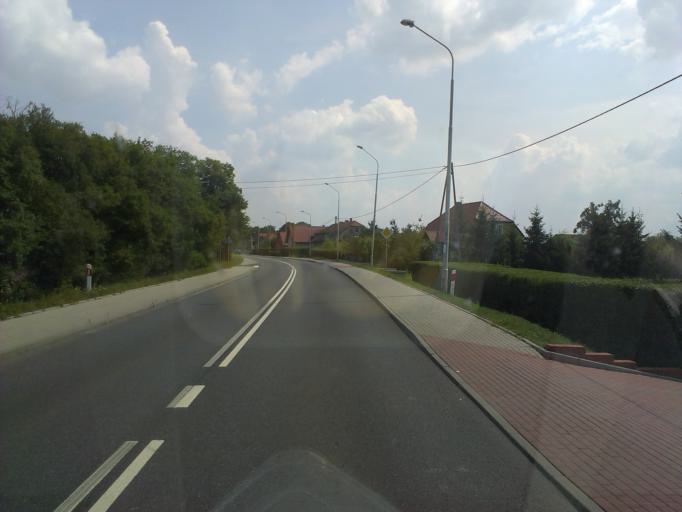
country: PL
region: Lower Silesian Voivodeship
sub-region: Powiat sredzki
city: Malczyce
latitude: 51.2032
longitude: 16.4758
